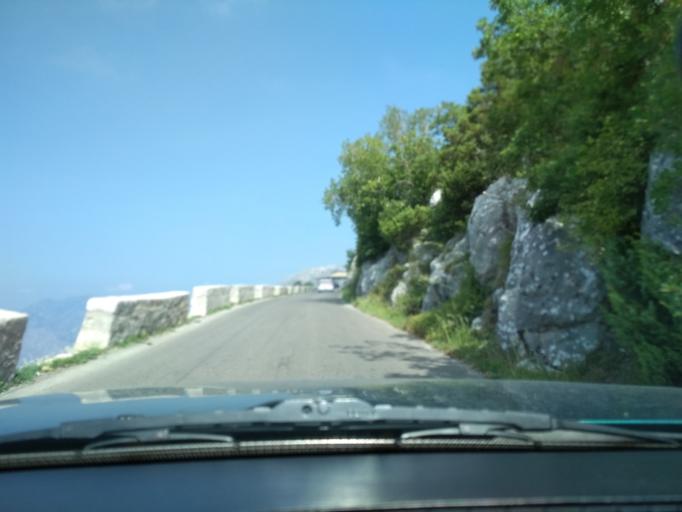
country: ME
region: Kotor
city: Kotor
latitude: 42.4082
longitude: 18.7863
